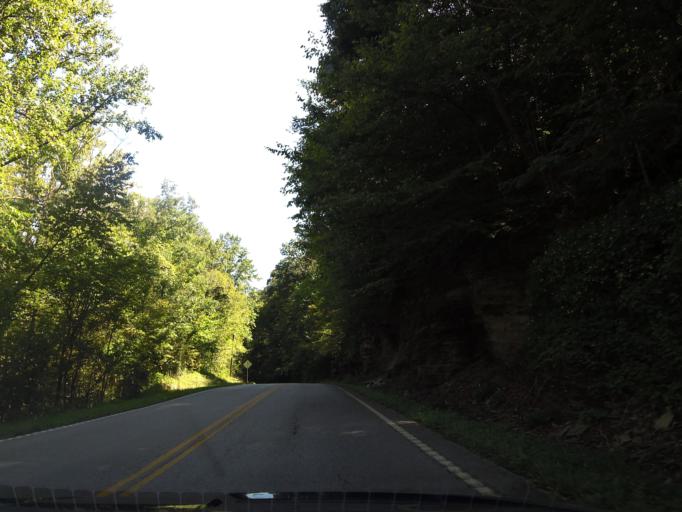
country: US
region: Kentucky
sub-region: Leslie County
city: Hyden
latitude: 37.1653
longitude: -83.5331
